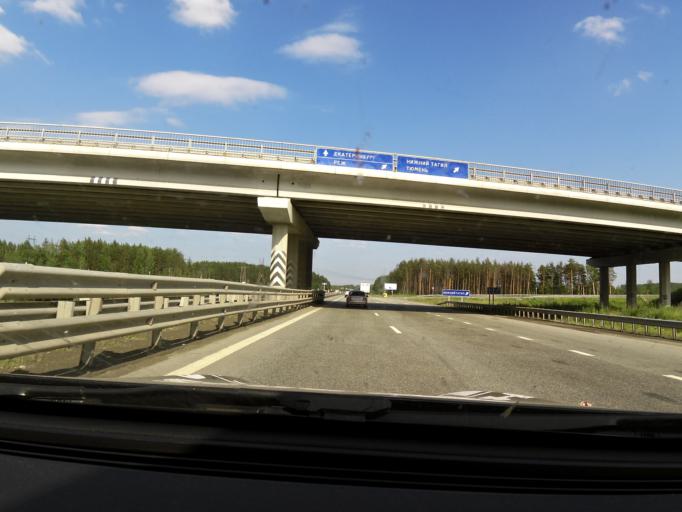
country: RU
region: Sverdlovsk
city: Severka
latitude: 56.8331
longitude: 60.3203
